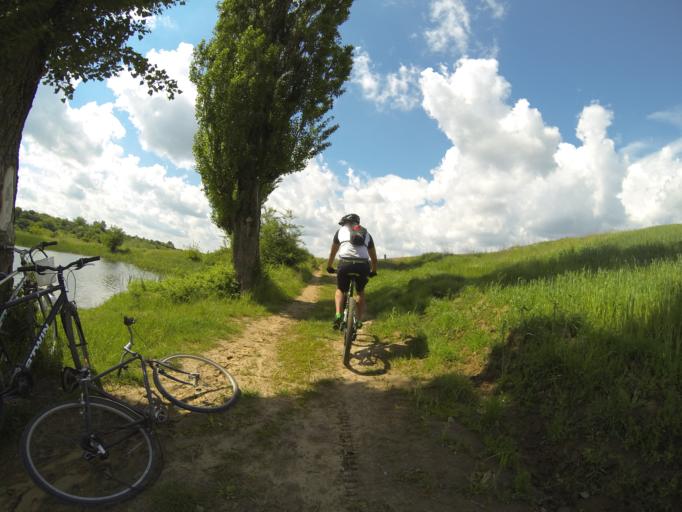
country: RO
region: Dolj
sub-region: Comuna Malu Mare
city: Preajba
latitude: 44.2675
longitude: 23.8526
